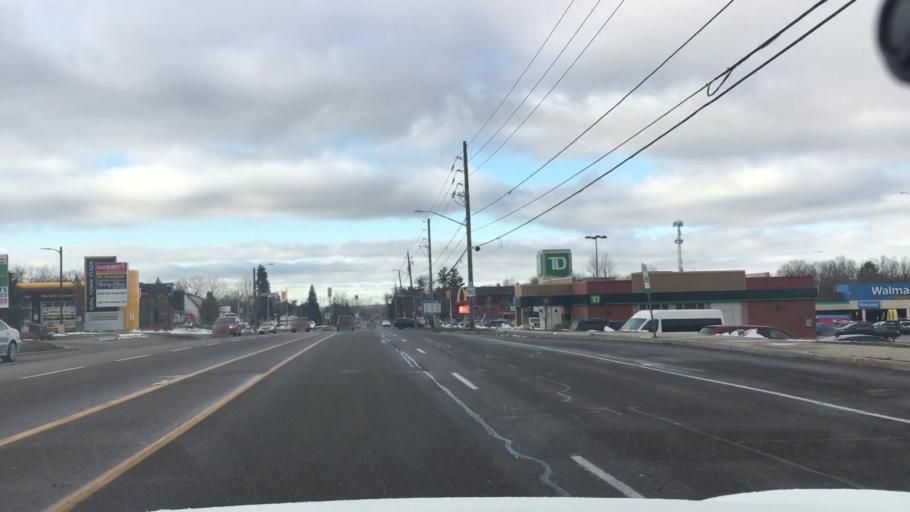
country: CA
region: Ontario
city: Oshawa
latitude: 43.9065
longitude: -78.8140
